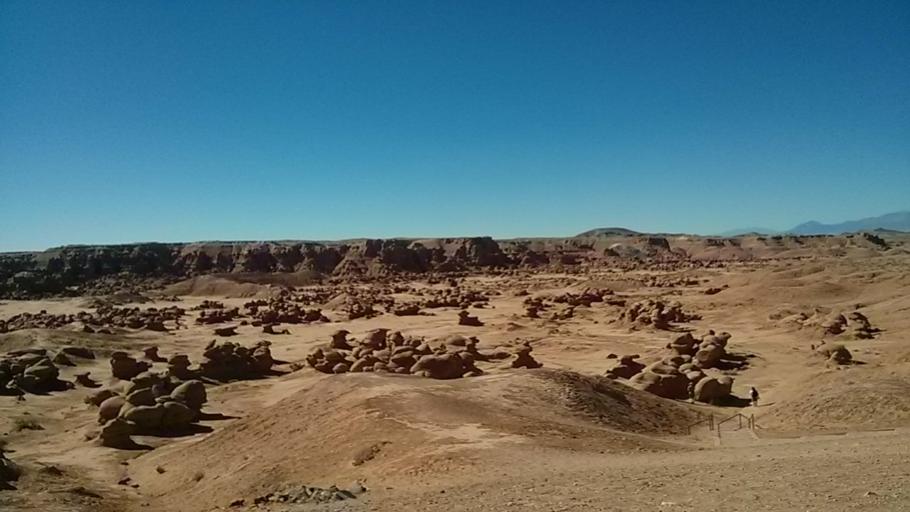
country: US
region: Utah
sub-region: Emery County
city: Ferron
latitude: 38.5641
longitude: -110.7032
